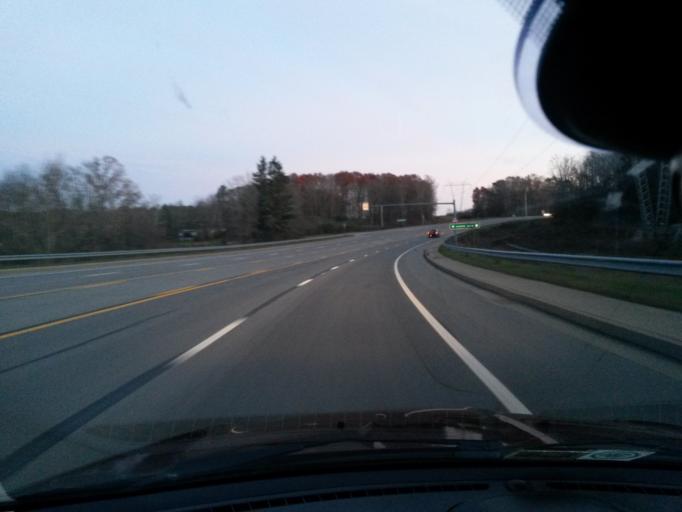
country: US
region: West Virginia
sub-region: Raleigh County
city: Stanaford
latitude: 37.7870
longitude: -81.1538
